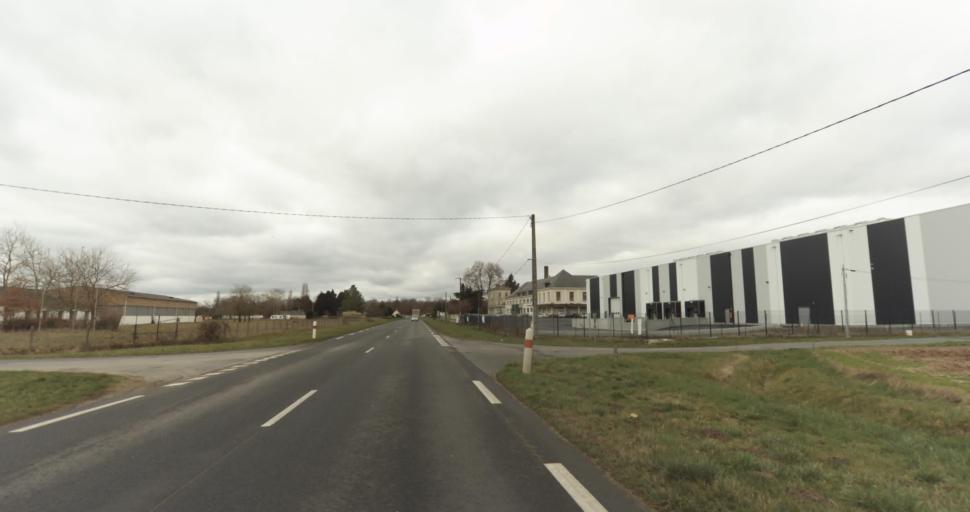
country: FR
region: Pays de la Loire
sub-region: Departement de Maine-et-Loire
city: Allonnes
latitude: 47.3004
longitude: -0.0069
